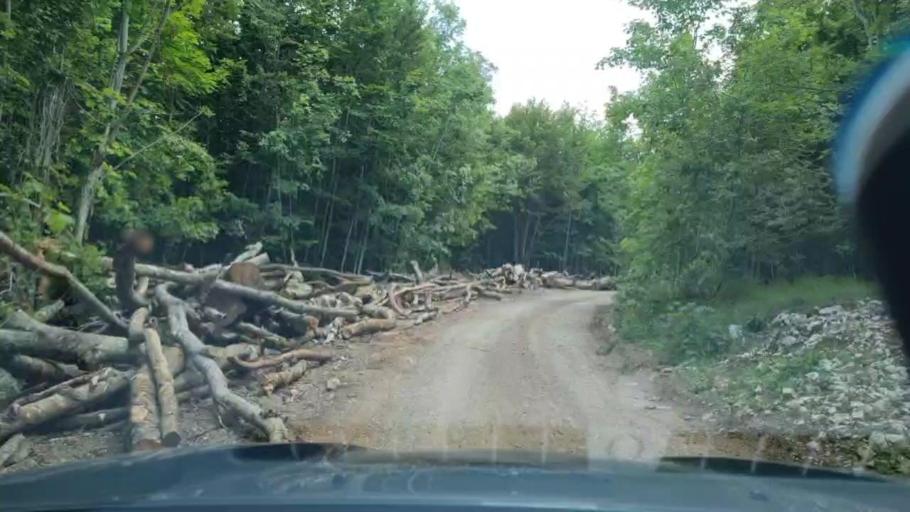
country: BA
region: Federation of Bosnia and Herzegovina
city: Bosansko Grahovo
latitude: 44.3208
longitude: 16.2468
